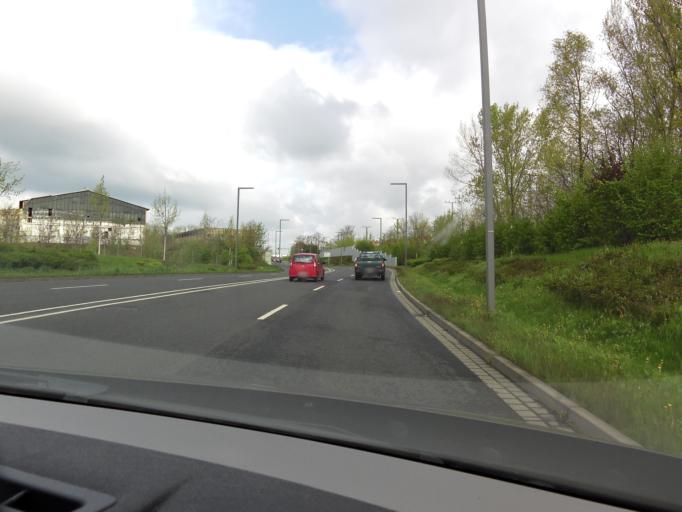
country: DE
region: Saxony
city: Leipzig
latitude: 51.3784
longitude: 12.3262
